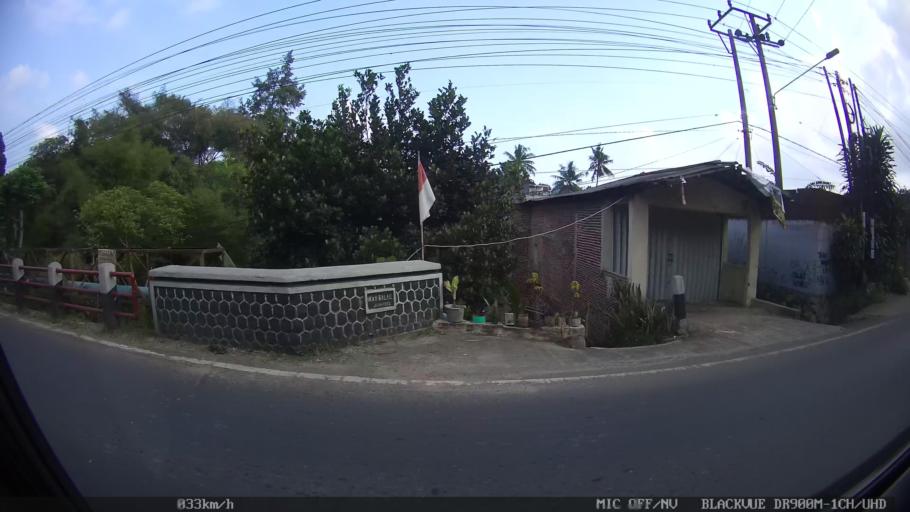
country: ID
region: Lampung
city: Kedaton
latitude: -5.3936
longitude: 105.2225
